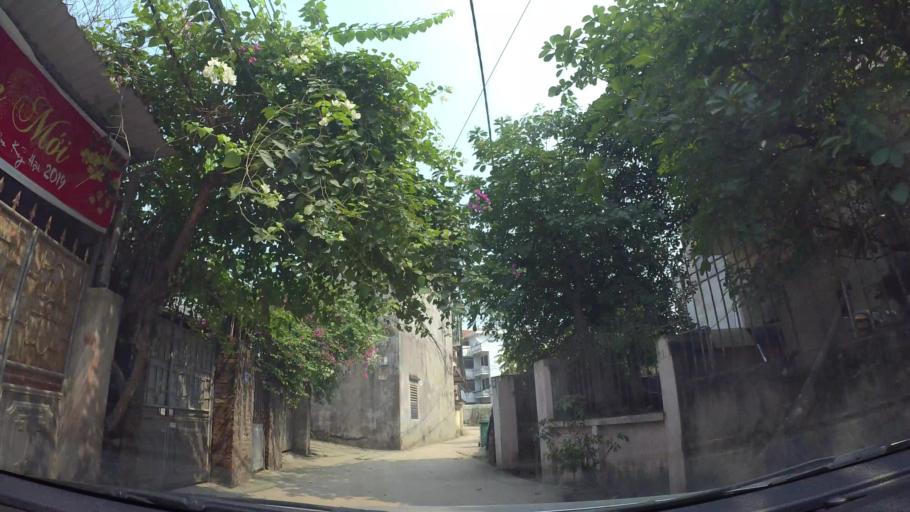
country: VN
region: Ha Noi
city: Cau Dien
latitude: 21.0033
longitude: 105.7610
